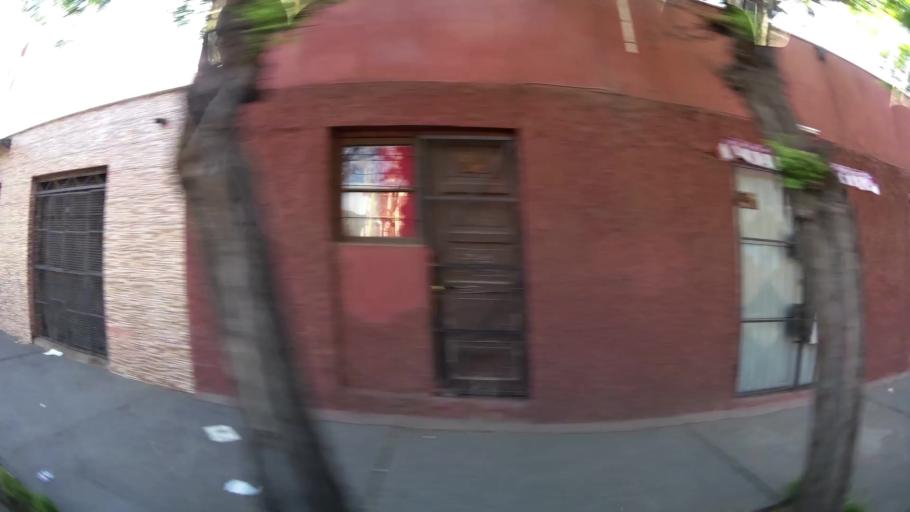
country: CL
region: Santiago Metropolitan
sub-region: Provincia de Santiago
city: Santiago
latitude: -33.3820
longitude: -70.6724
